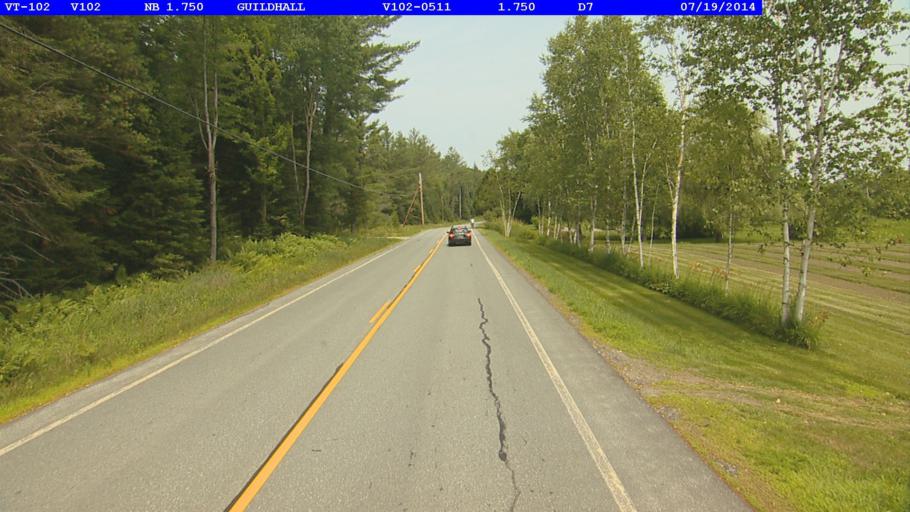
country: US
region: New Hampshire
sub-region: Coos County
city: Lancaster
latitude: 44.5206
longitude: -71.5950
